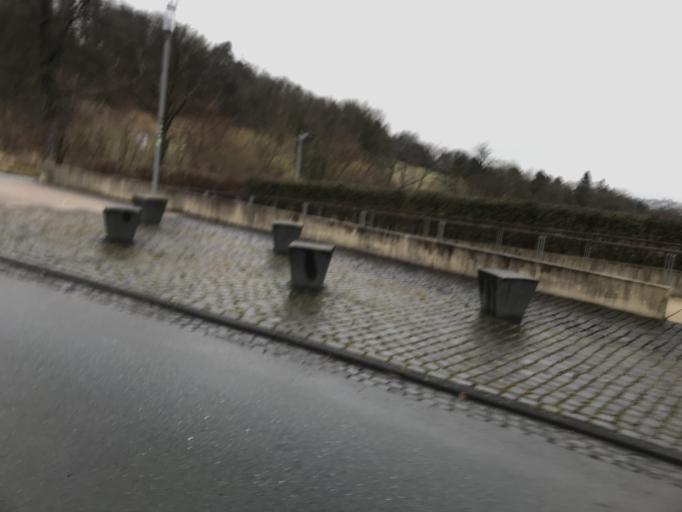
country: DE
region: Hesse
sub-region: Regierungsbezirk Kassel
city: Bad Wildungen
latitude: 51.1154
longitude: 9.1077
